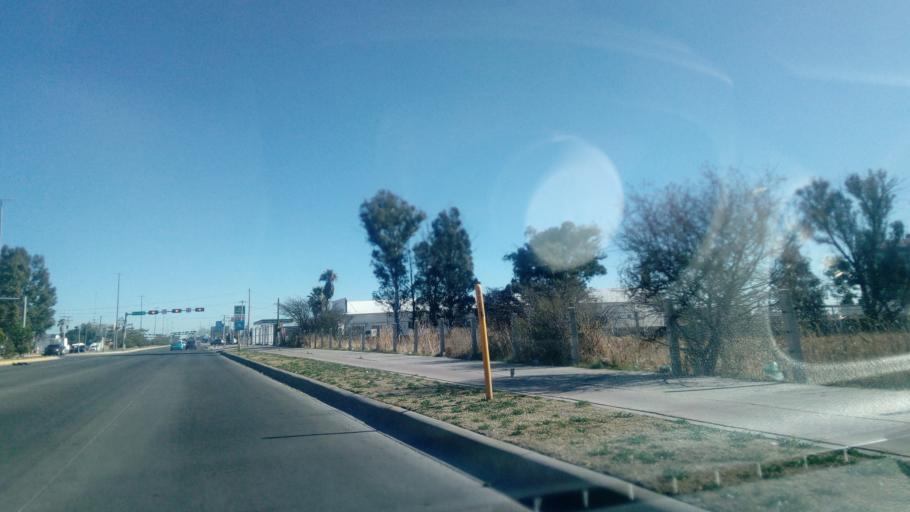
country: MX
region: Durango
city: Victoria de Durango
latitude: 24.0721
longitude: -104.5957
